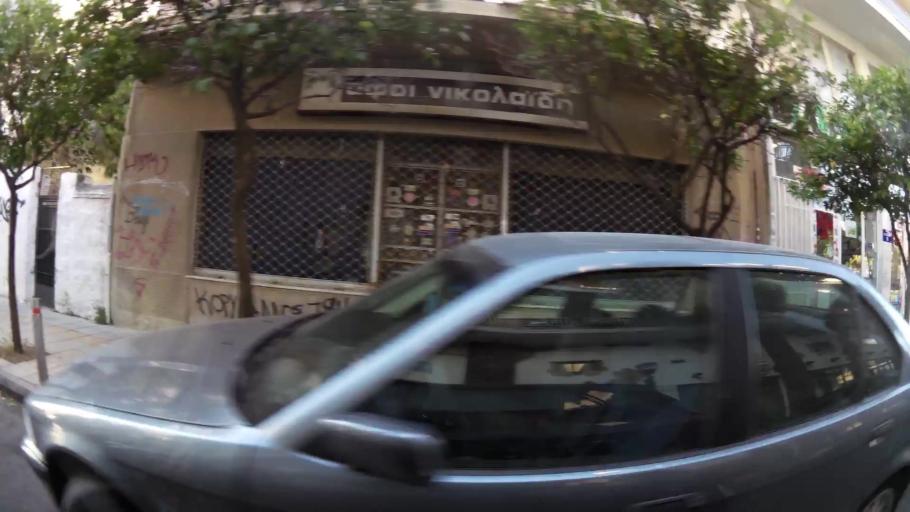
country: GR
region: Attica
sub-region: Nomos Piraios
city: Nikaia
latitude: 37.9748
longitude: 23.6561
